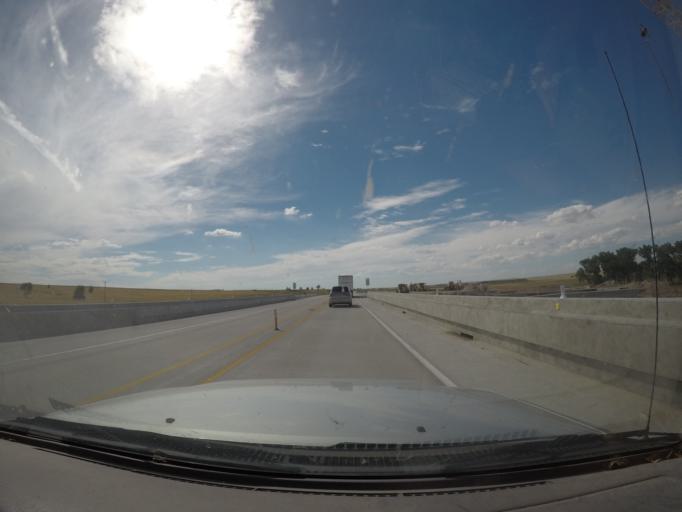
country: US
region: Nebraska
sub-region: Deuel County
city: Chappell
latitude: 41.0910
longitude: -102.5153
